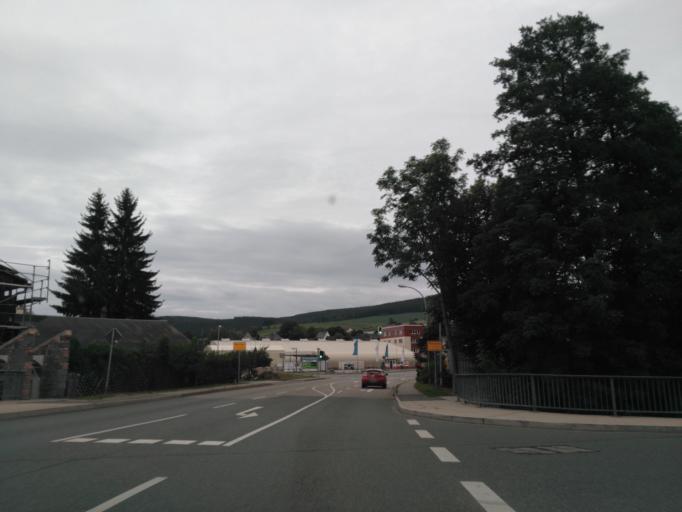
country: DE
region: Saxony
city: Raschau
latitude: 50.5288
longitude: 12.8192
